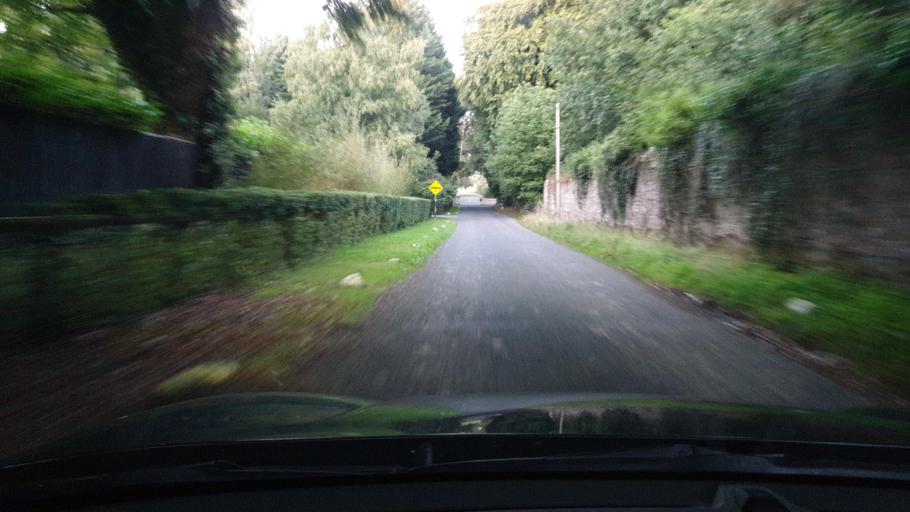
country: IE
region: Leinster
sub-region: Kildare
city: Prosperous
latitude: 53.3482
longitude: -6.7518
